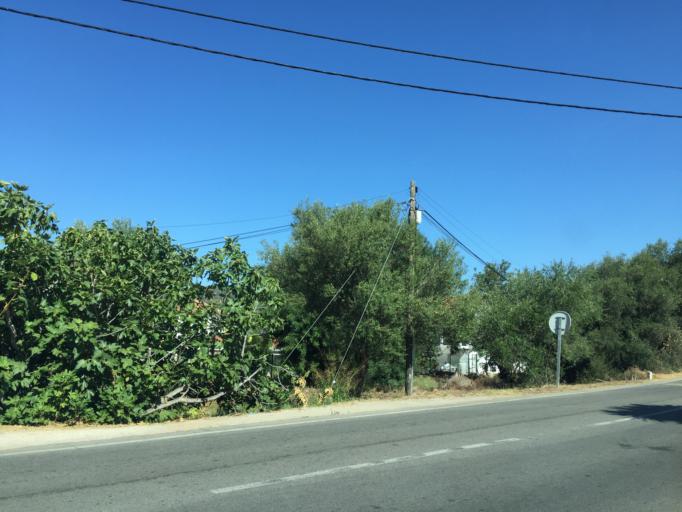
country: PT
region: Faro
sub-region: Loule
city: Almancil
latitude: 37.1006
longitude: -8.0421
